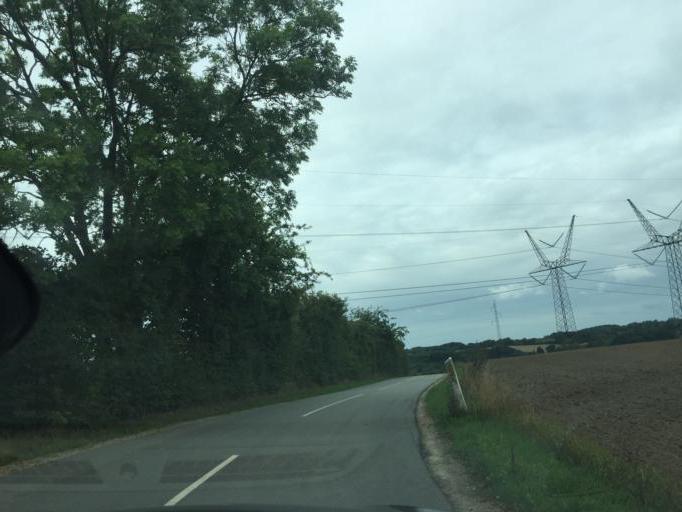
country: DK
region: South Denmark
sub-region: Assens Kommune
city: Tommerup Stationsby
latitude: 55.3842
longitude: 10.1767
